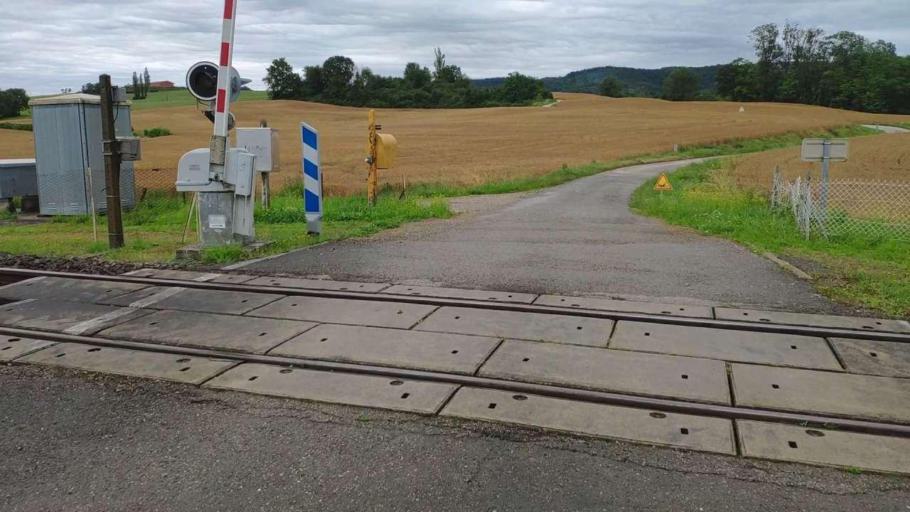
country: FR
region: Franche-Comte
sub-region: Departement du Jura
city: Perrigny
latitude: 46.7796
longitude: 5.5918
